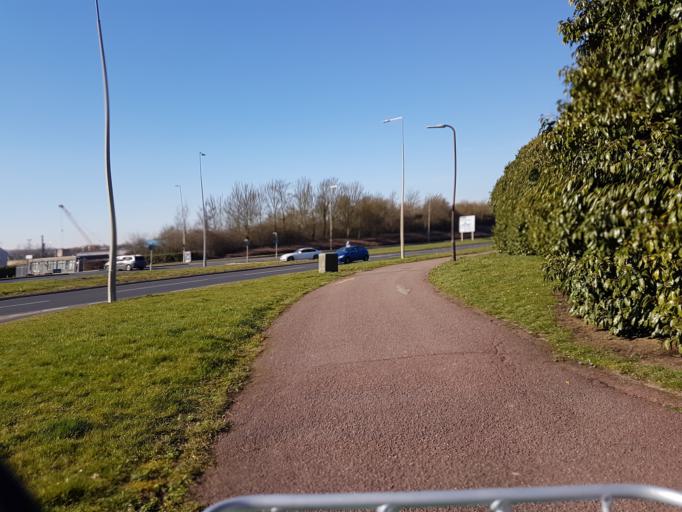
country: GB
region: England
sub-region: Milton Keynes
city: Milton Keynes
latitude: 52.0234
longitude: -0.7547
